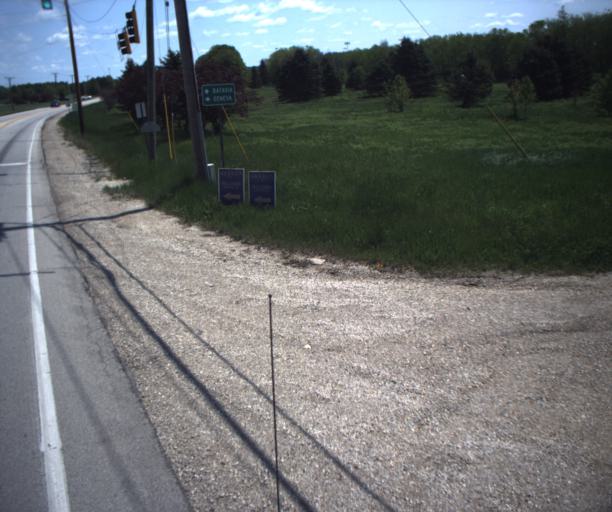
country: US
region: Illinois
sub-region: Kane County
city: Elburn
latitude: 41.8469
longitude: -88.4022
